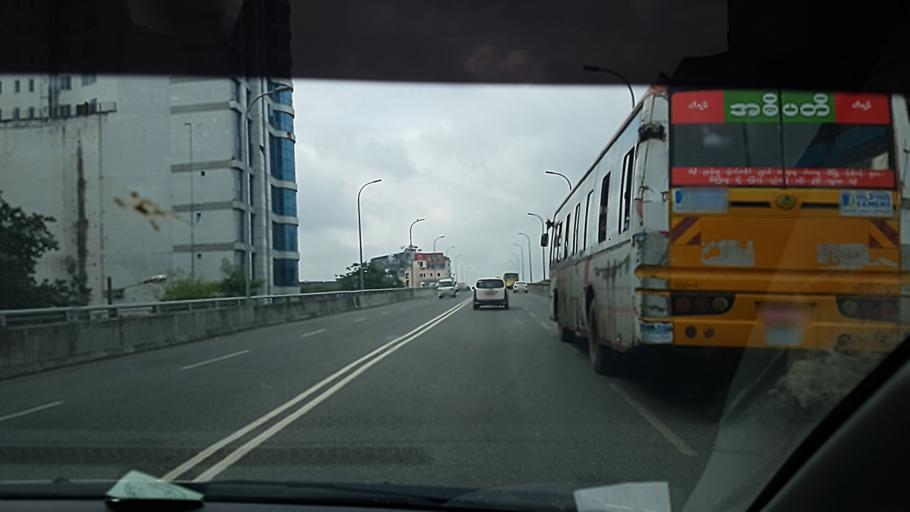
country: MM
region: Yangon
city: Yangon
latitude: 16.8052
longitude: 96.1369
